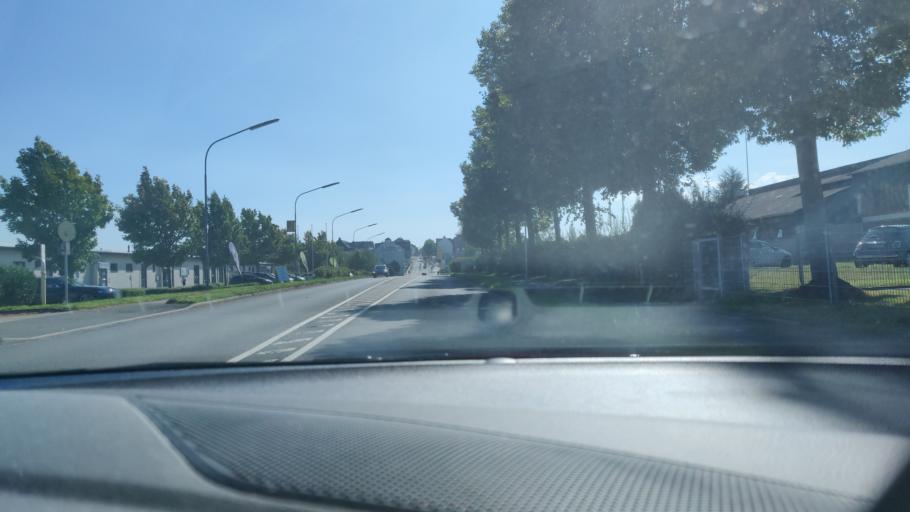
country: DE
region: North Rhine-Westphalia
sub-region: Regierungsbezirk Dusseldorf
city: Velbert
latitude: 51.3201
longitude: 7.0617
